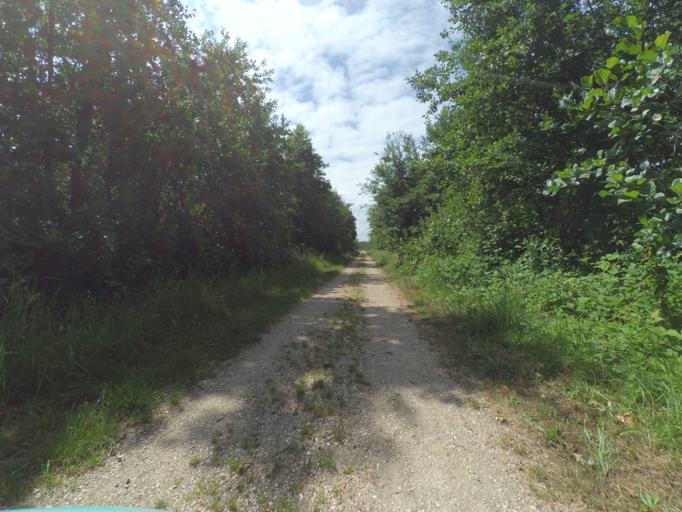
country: NL
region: Zeeland
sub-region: Gemeente Noord-Beveland
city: Kamperland
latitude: 51.5340
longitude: 3.7315
